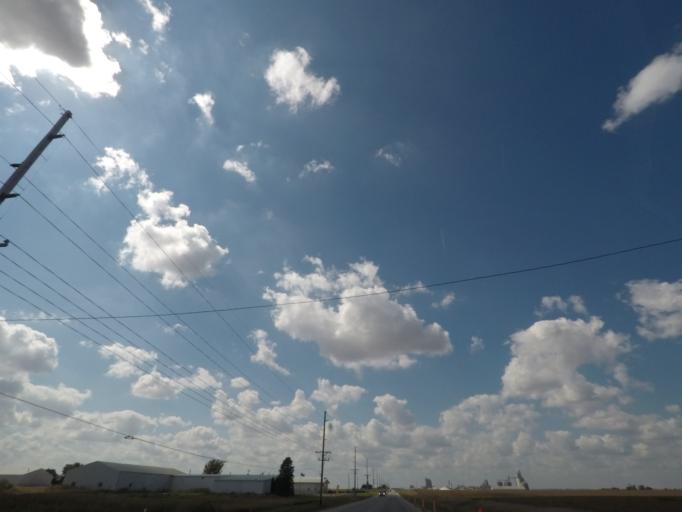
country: US
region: Iowa
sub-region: Story County
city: Nevada
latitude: 42.0230
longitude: -93.4831
